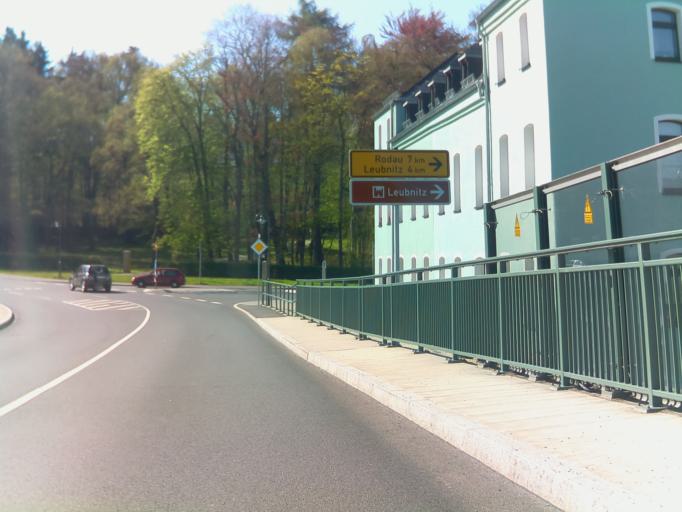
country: DE
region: Saxony
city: Mehltheuer
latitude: 50.5454
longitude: 12.0414
